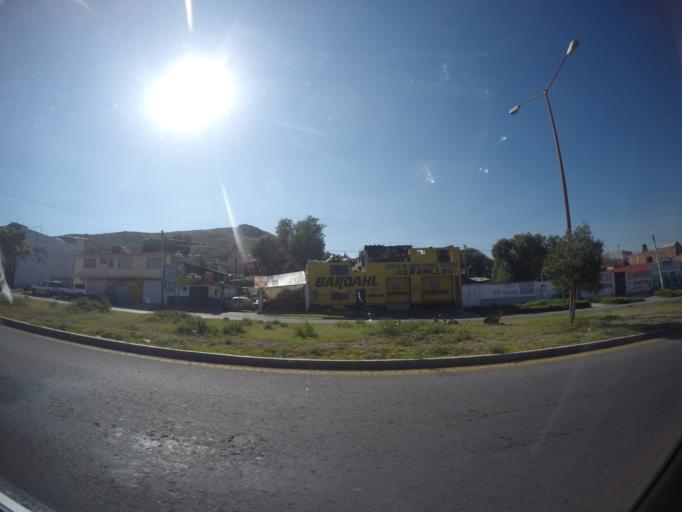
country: MX
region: Hidalgo
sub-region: Mineral de la Reforma
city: Rio de la Soledad
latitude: 20.1159
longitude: -98.7133
